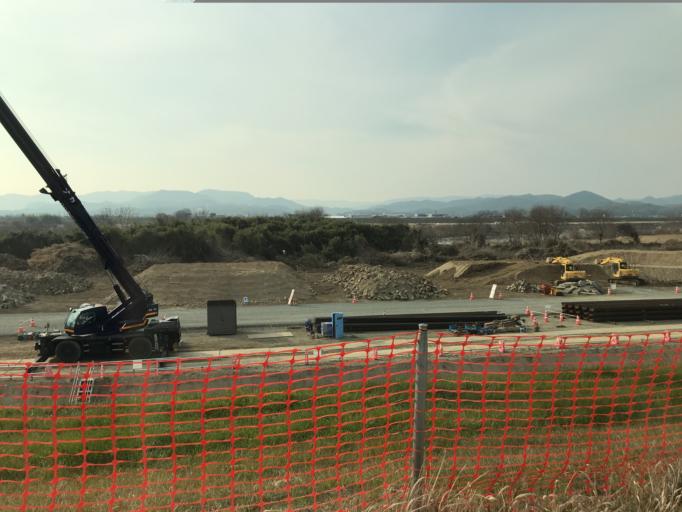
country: JP
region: Okayama
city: Soja
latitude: 34.6355
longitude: 133.7308
